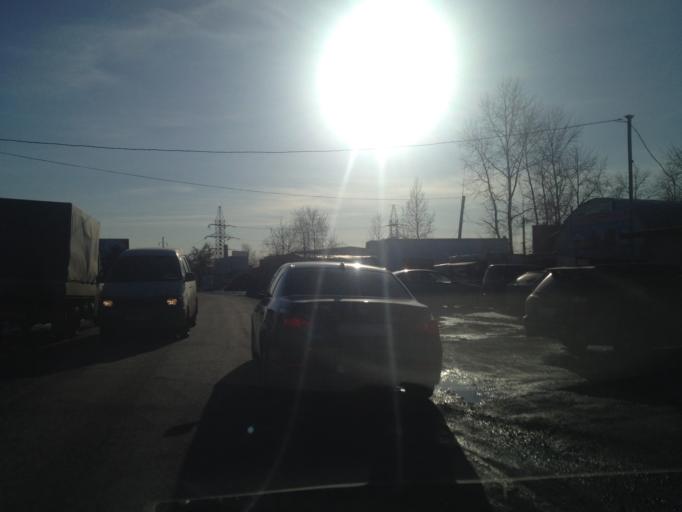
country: RU
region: Sverdlovsk
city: Yekaterinburg
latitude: 56.8794
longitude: 60.5493
